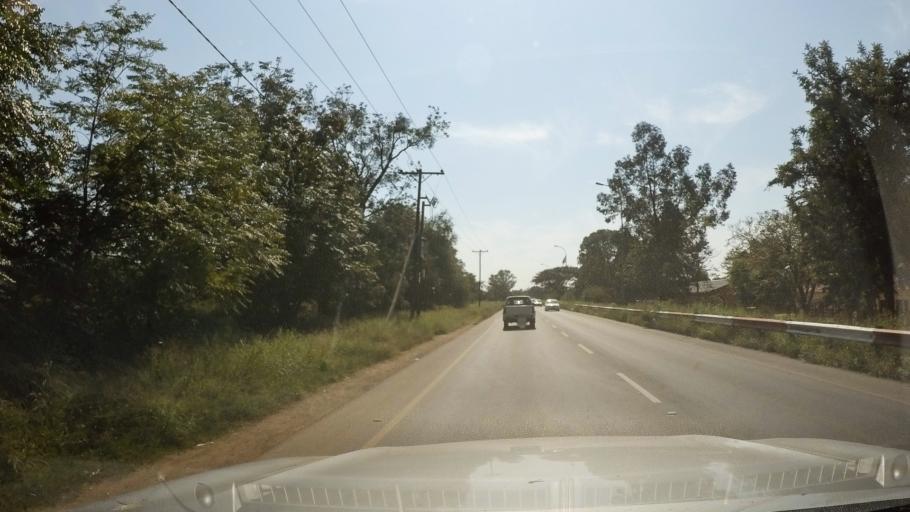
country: BW
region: South East
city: Lobatse
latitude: -25.2196
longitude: 25.6801
